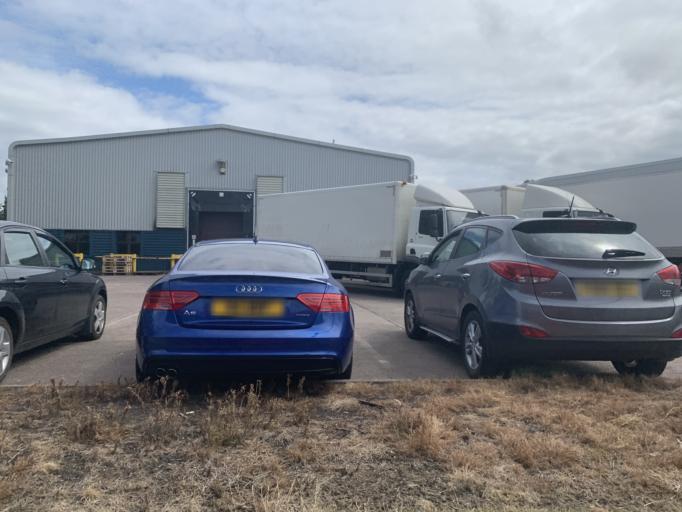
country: GB
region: Scotland
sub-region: Renfrewshire
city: Inchinnan
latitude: 55.8655
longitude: -4.4260
